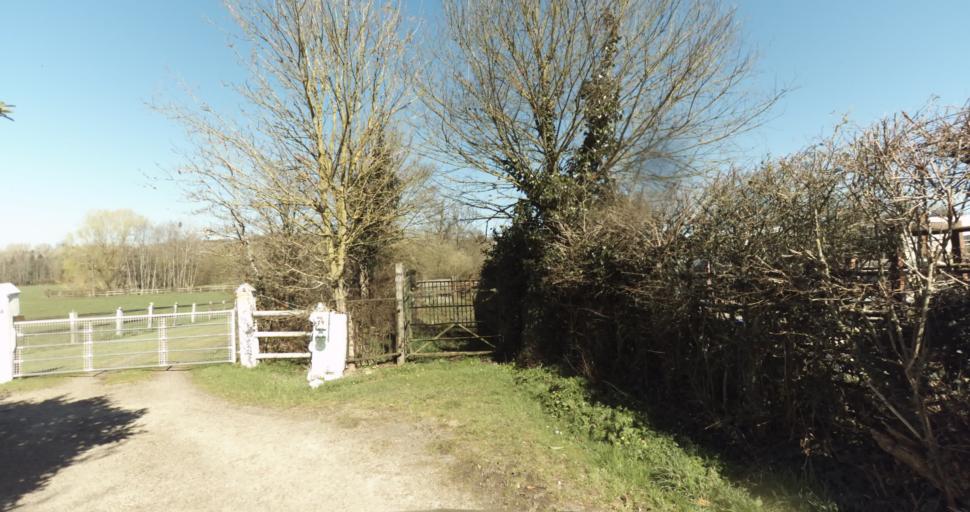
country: FR
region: Lower Normandy
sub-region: Departement du Calvados
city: Livarot
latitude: 49.0200
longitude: 0.0751
